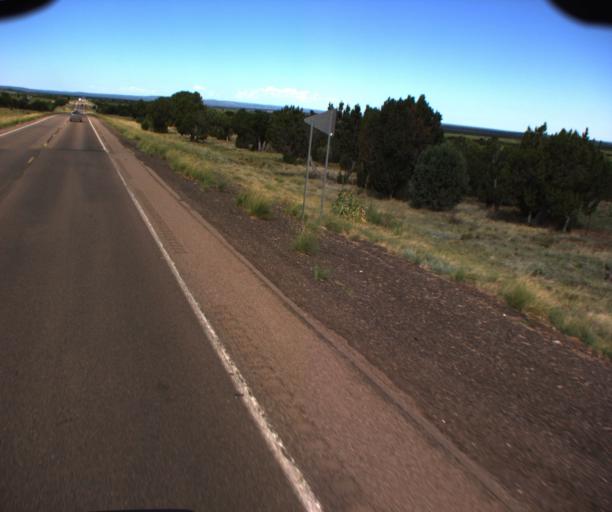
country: US
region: Arizona
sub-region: Navajo County
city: White Mountain Lake
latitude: 34.2729
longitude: -109.9116
